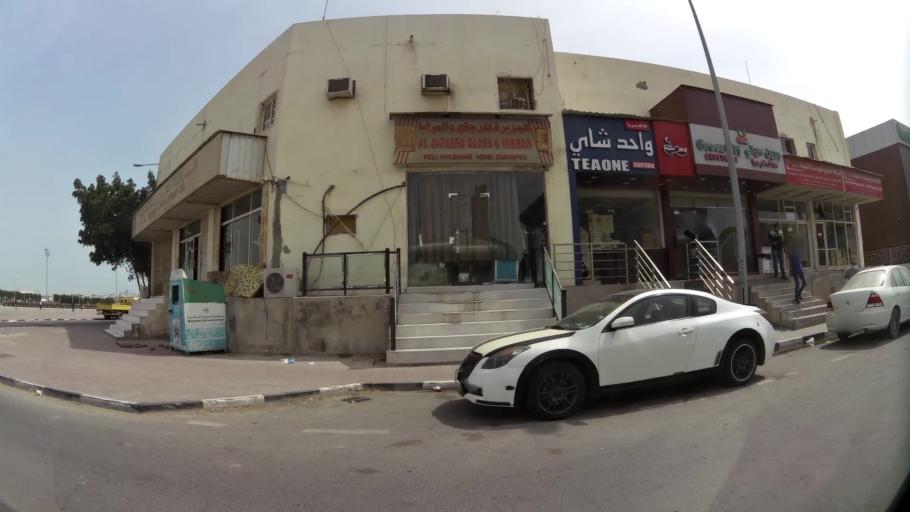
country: QA
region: Baladiyat ad Dawhah
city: Doha
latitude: 25.2676
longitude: 51.4860
